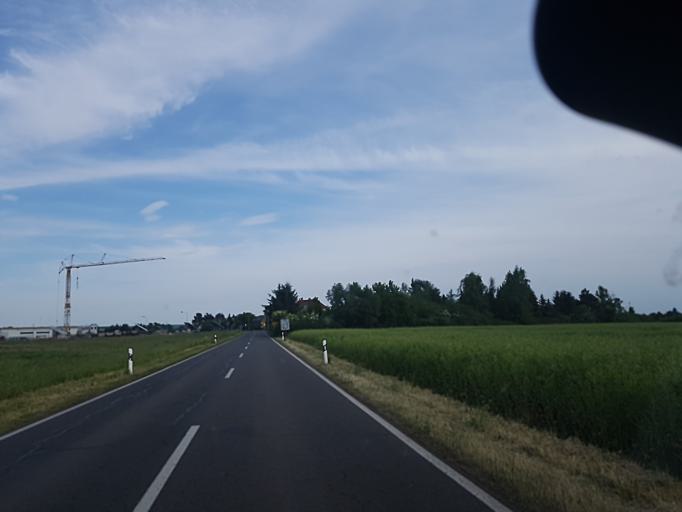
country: DE
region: Saxony-Anhalt
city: Zahna
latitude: 51.9276
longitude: 12.7774
